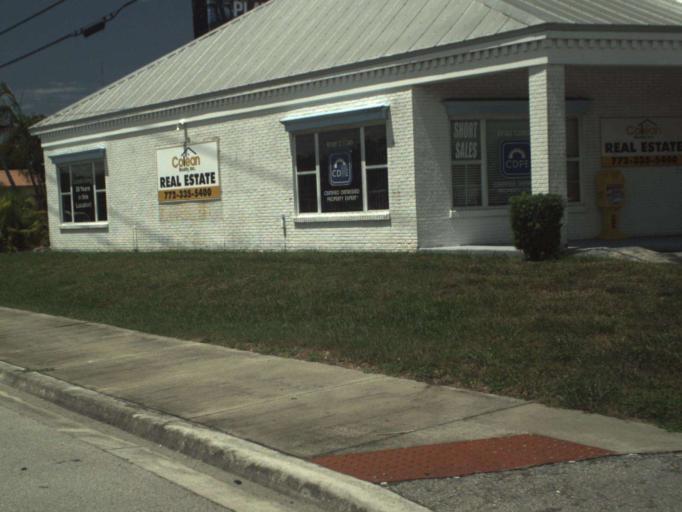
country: US
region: Florida
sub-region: Martin County
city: North River Shores
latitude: 27.2664
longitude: -80.2854
